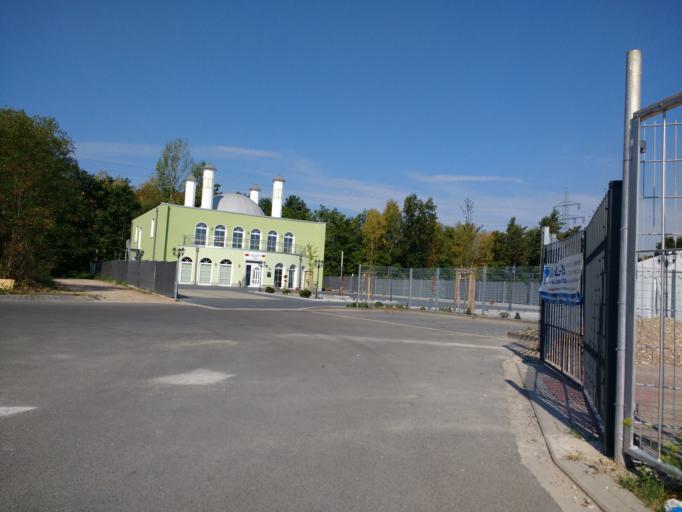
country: DE
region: Lower Saxony
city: Gifhorn
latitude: 52.4601
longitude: 10.5356
